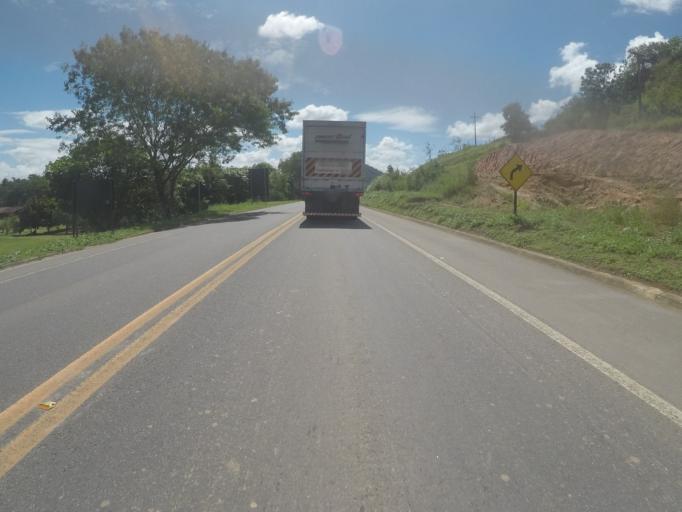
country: BR
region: Espirito Santo
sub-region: Viana
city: Viana
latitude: -20.4291
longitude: -40.4598
